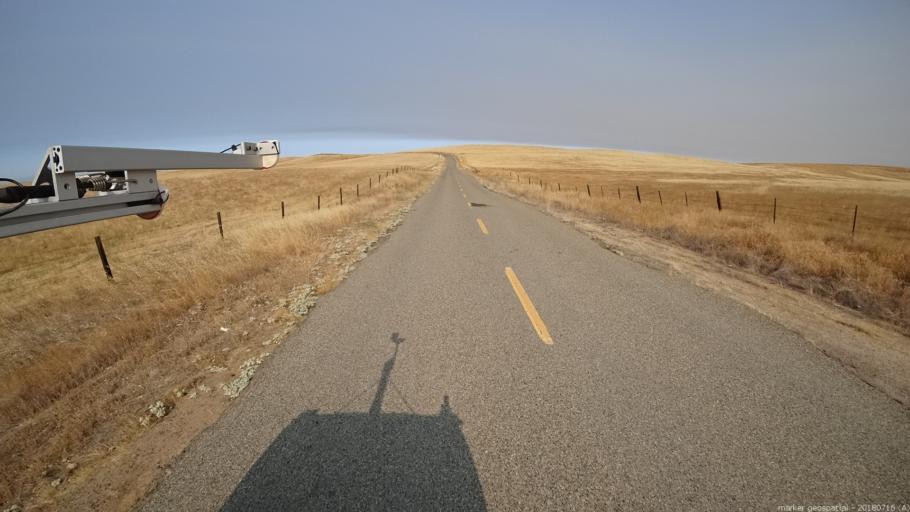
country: US
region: California
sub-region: Madera County
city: Madera Acres
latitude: 37.1192
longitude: -119.9892
